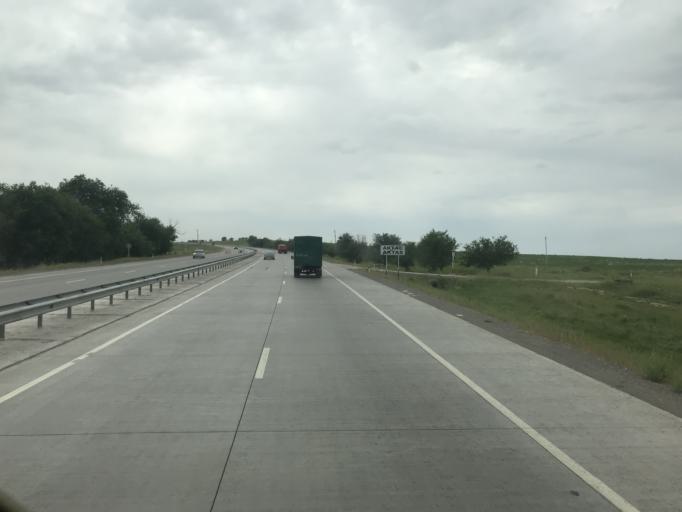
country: KZ
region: Ongtustik Qazaqstan
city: Shymkent
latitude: 42.2064
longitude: 69.5132
